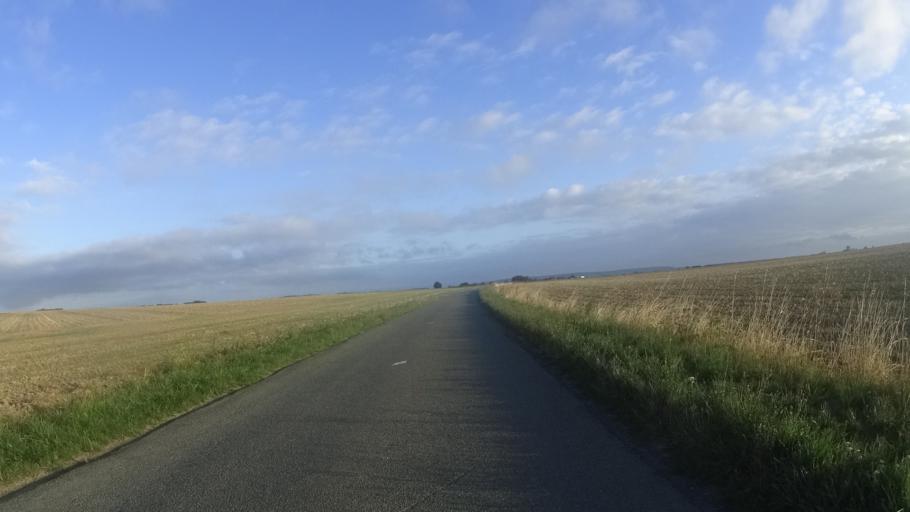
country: FR
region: Picardie
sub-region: Departement de l'Oise
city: Chamant
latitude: 49.1936
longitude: 2.6694
